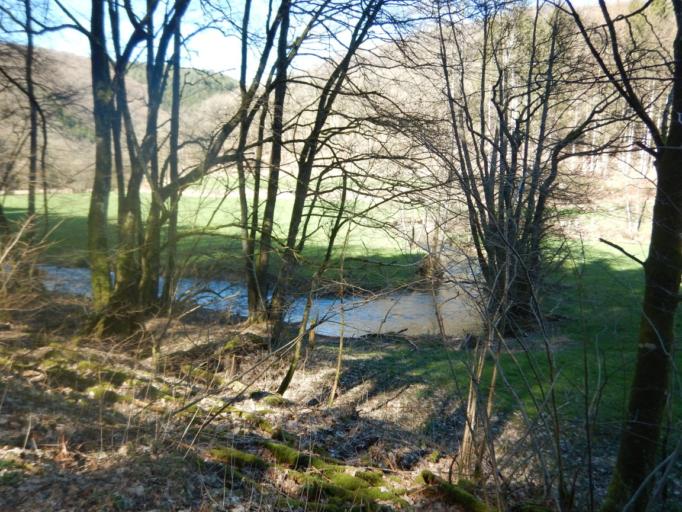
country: LU
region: Diekirch
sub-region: Canton de Wiltz
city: Wilwerwiltz
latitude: 49.9715
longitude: 5.9710
